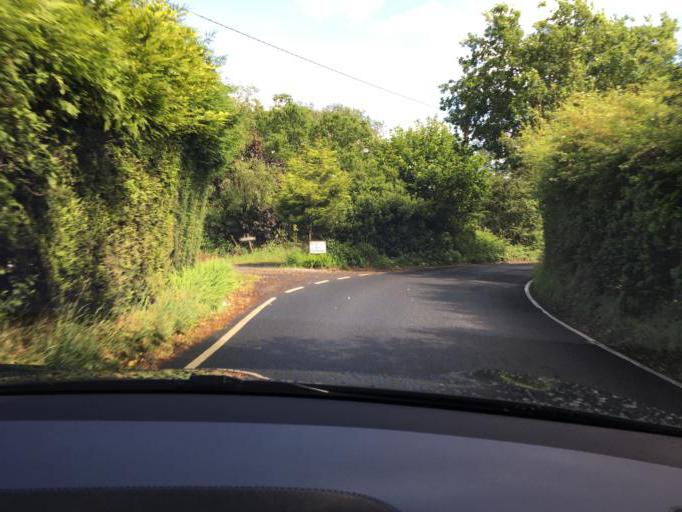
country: GB
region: England
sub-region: Borough of Stockport
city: Marple
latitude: 53.3811
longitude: -2.0753
